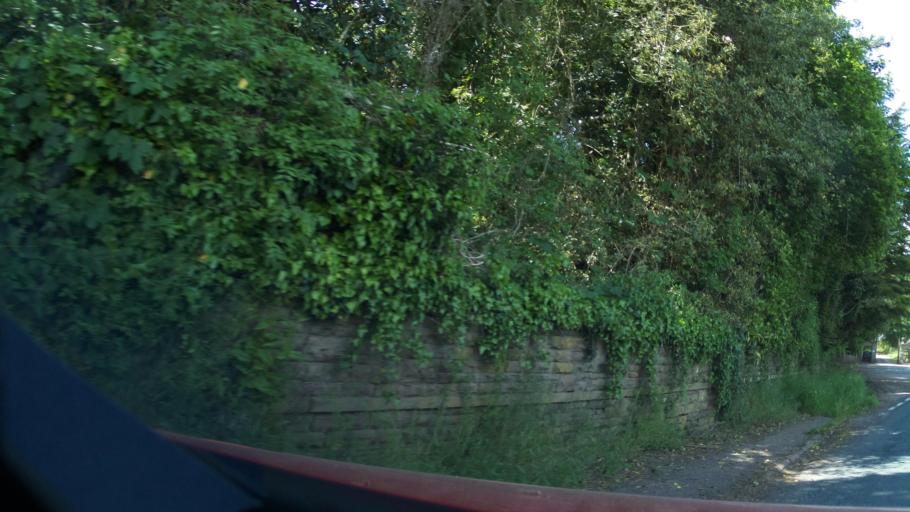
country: GB
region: Wales
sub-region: Monmouthshire
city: Monmouth
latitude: 51.8256
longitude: -2.7470
